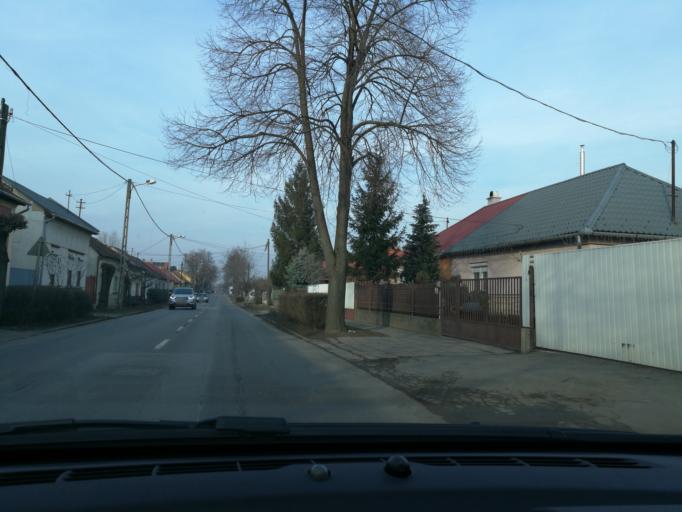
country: HU
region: Szabolcs-Szatmar-Bereg
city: Nyiregyhaza
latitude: 47.9531
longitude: 21.6942
